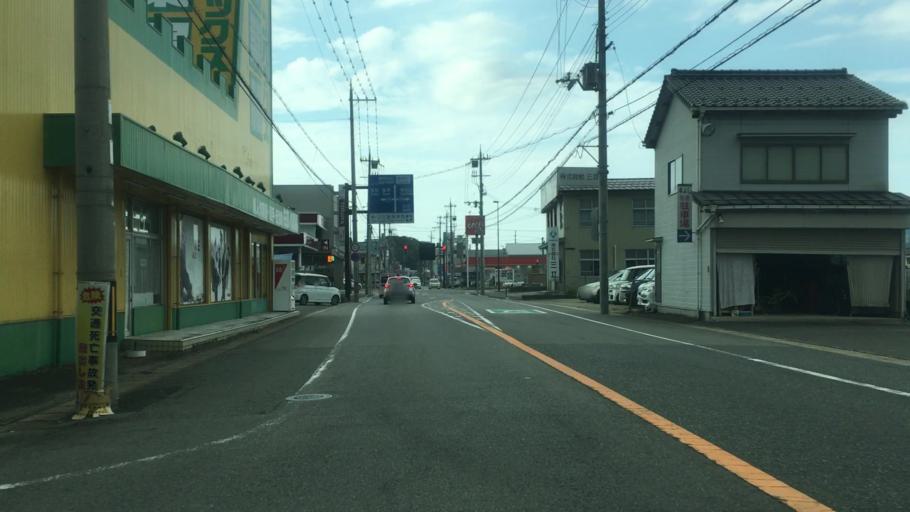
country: JP
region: Hyogo
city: Toyooka
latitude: 35.5271
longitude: 134.8208
